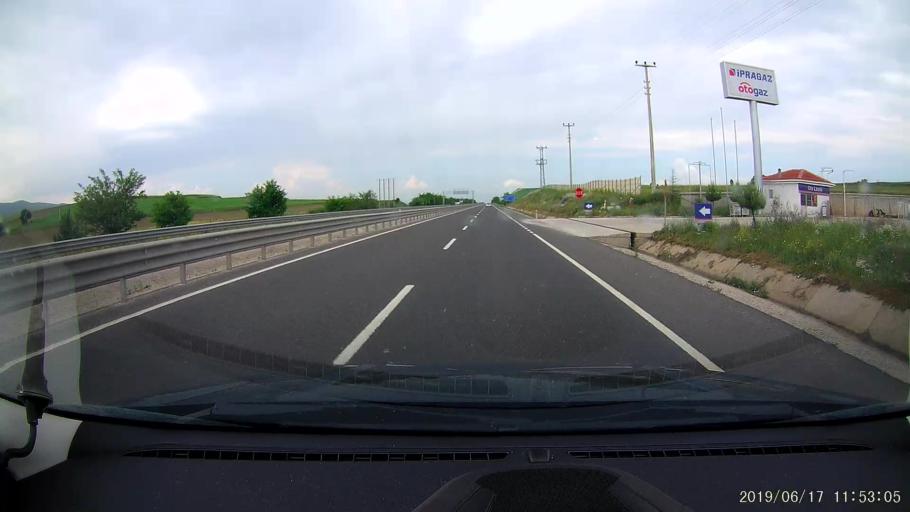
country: TR
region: Cankiri
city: Atkaracalar
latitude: 40.8061
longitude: 33.0684
